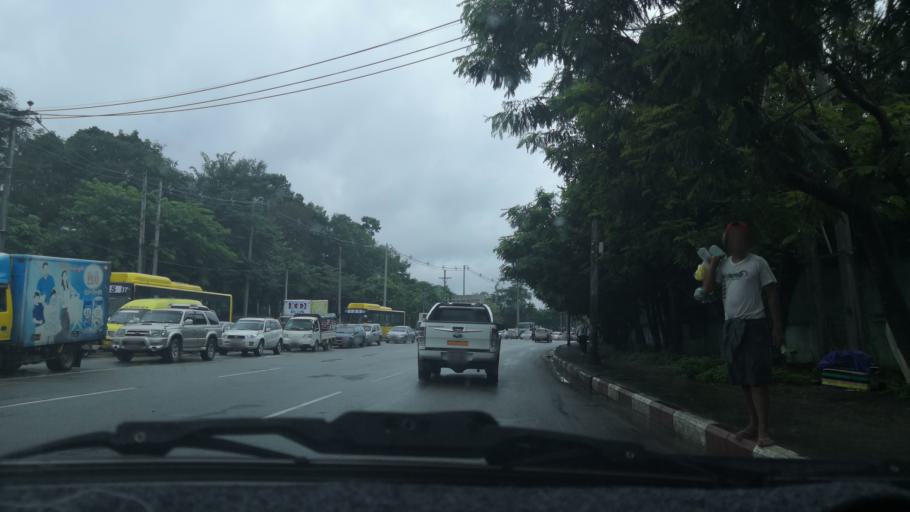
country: MM
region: Yangon
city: Yangon
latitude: 16.8902
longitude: 96.1208
